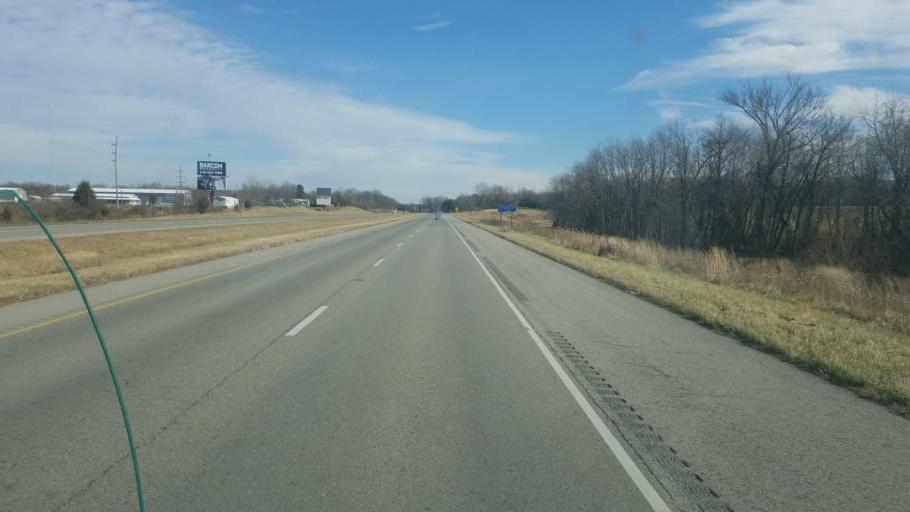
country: US
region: Illinois
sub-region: Williamson County
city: Marion
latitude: 37.7296
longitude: -88.8334
